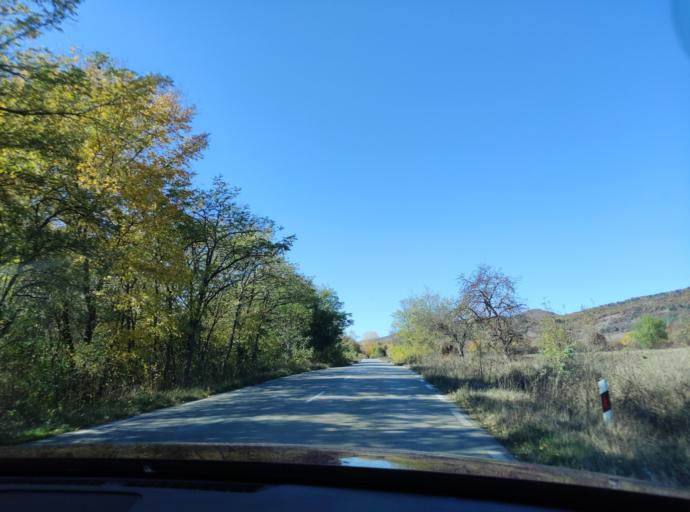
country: BG
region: Montana
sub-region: Obshtina Chiprovtsi
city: Chiprovtsi
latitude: 43.4267
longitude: 23.0064
